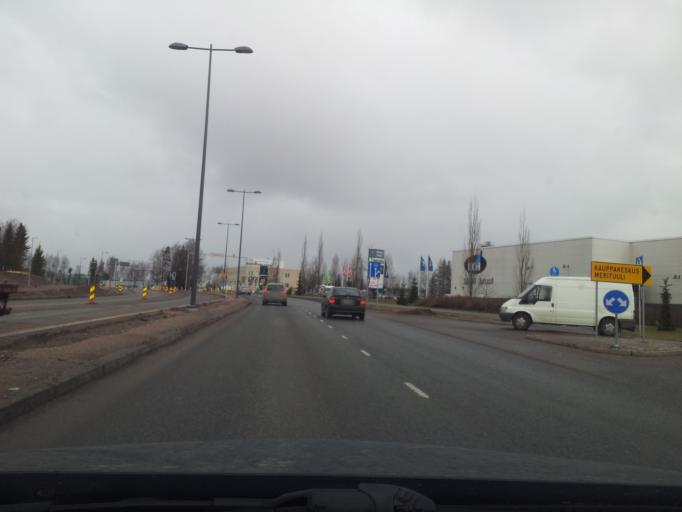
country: FI
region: Uusimaa
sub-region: Helsinki
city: Kauniainen
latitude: 60.1633
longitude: 24.7033
